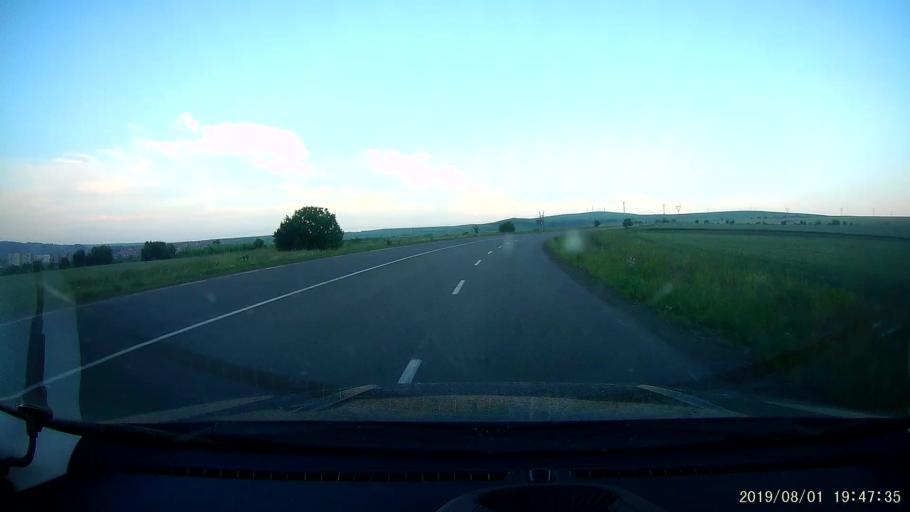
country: BG
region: Burgas
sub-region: Obshtina Karnobat
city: Karnobat
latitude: 42.6497
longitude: 26.9577
